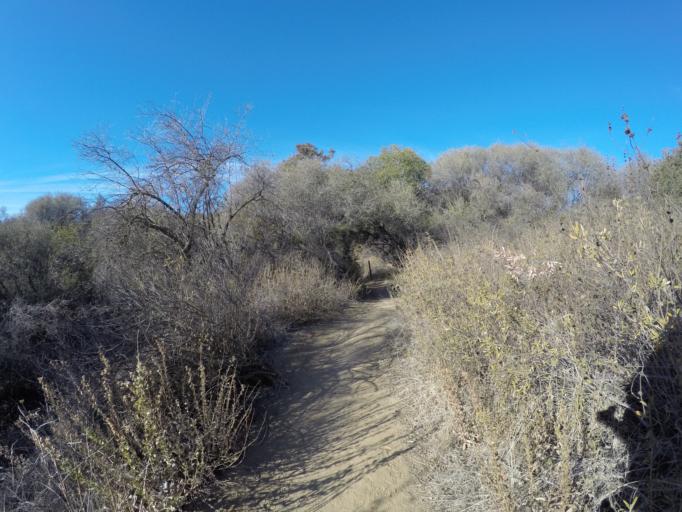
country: US
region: California
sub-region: Los Angeles County
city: Topanga
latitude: 34.1018
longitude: -118.5851
